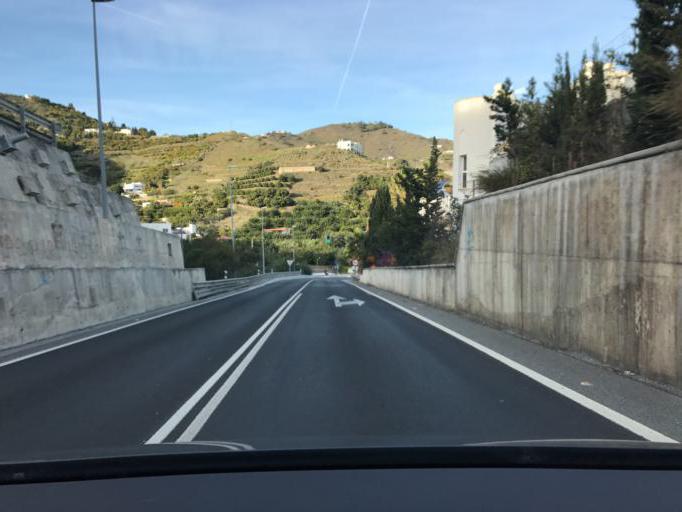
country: ES
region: Andalusia
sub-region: Provincia de Granada
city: Almunecar
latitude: 36.7472
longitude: -3.6657
